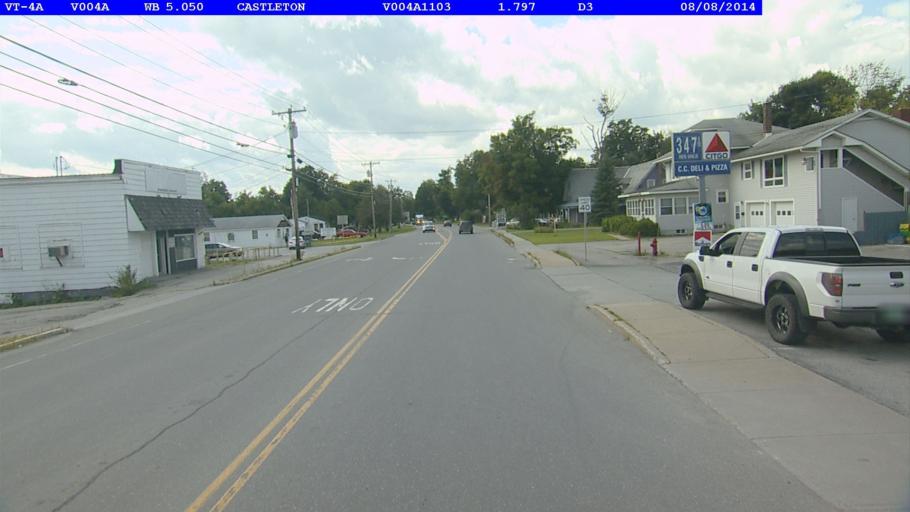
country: US
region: Vermont
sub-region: Rutland County
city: Castleton
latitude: 43.6085
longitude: -73.2088
